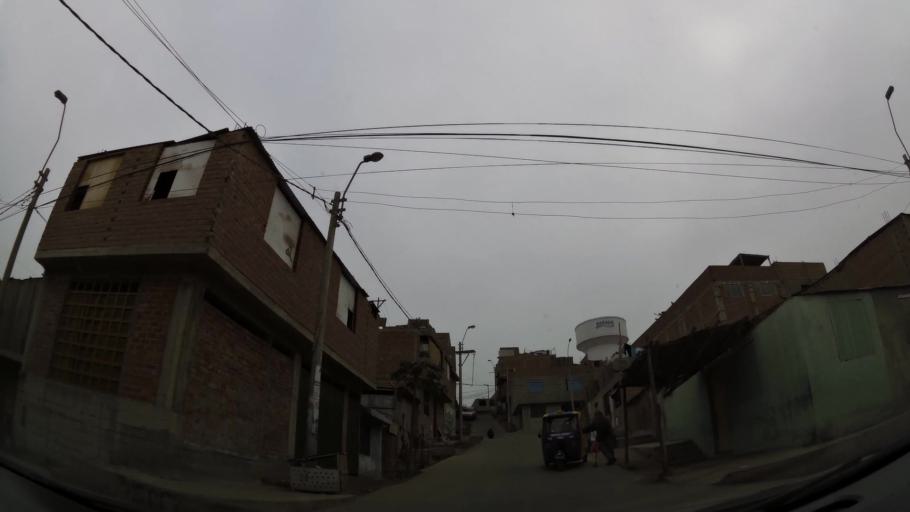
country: PE
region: Lima
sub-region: Lima
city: Surco
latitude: -12.1927
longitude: -76.9767
